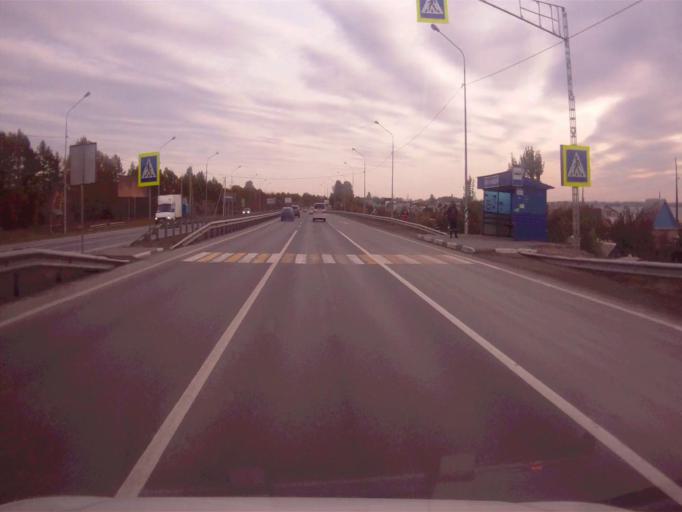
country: RU
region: Chelyabinsk
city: Novosineglazovskiy
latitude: 55.0314
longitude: 61.4458
